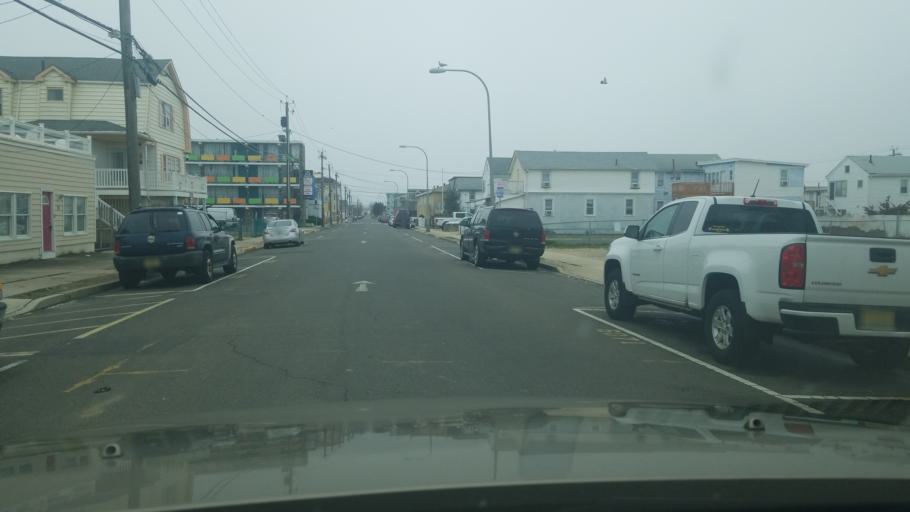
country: US
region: New Jersey
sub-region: Ocean County
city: Seaside Heights
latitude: 39.9377
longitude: -74.0723
